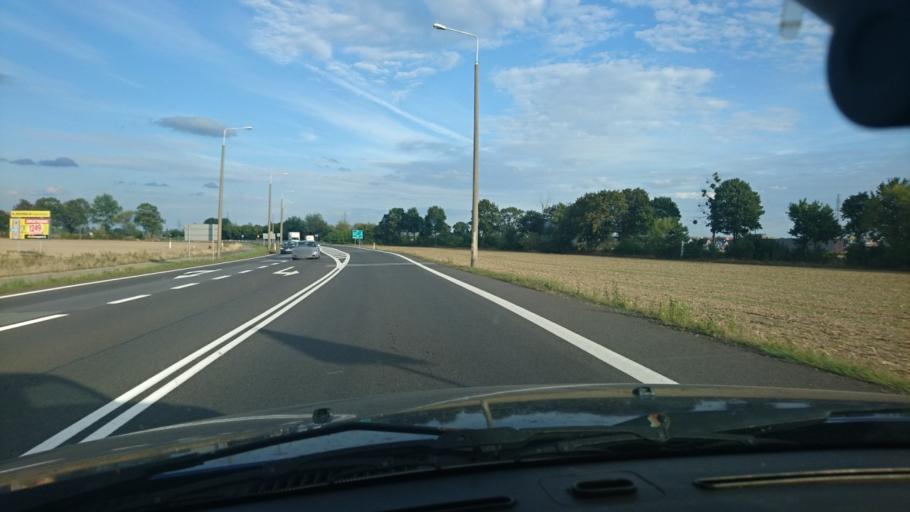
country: PL
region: Opole Voivodeship
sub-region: Powiat kluczborski
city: Kluczbork
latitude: 50.9924
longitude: 18.2122
